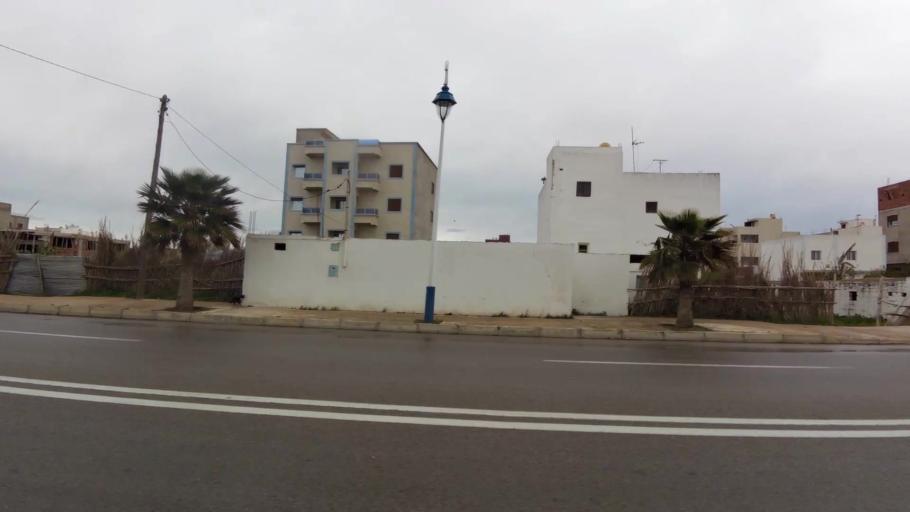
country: MA
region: Tanger-Tetouan
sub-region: Tetouan
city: Martil
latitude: 35.6302
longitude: -5.2891
